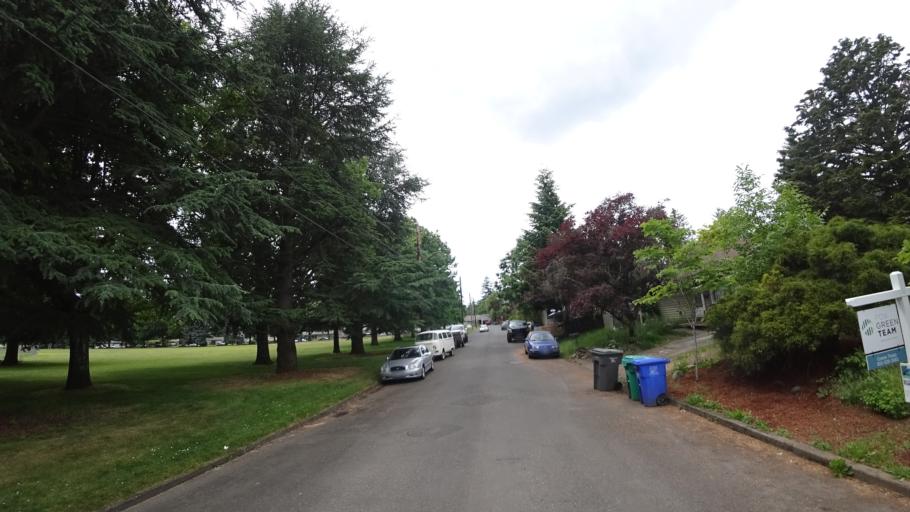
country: US
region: Oregon
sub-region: Multnomah County
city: Lents
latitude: 45.4867
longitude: -122.5589
